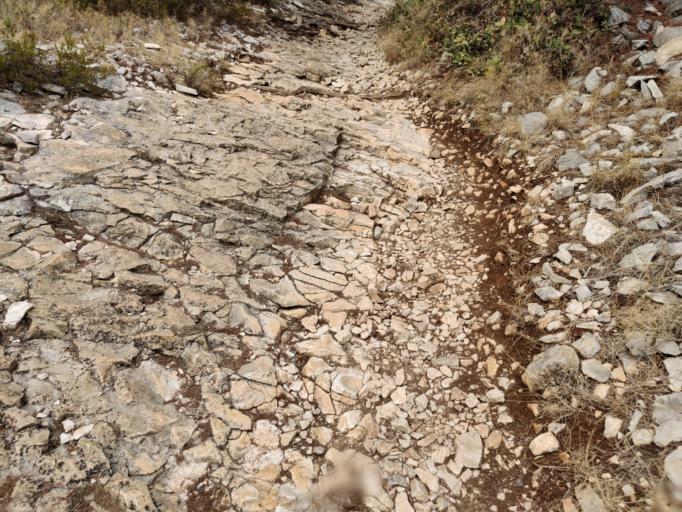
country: HR
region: Splitsko-Dalmatinska
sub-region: Grad Hvar
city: Hvar
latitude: 43.1642
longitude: 16.4542
